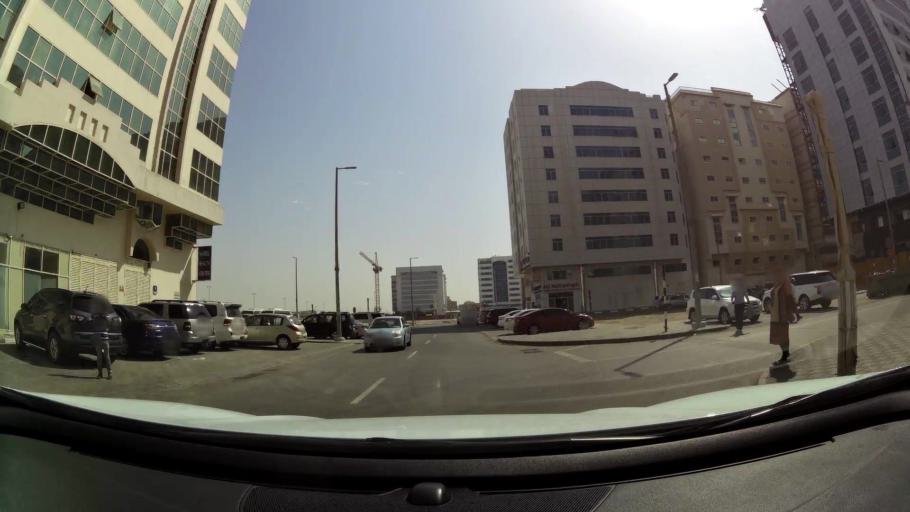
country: AE
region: Abu Dhabi
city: Abu Dhabi
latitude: 24.3444
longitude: 54.5370
